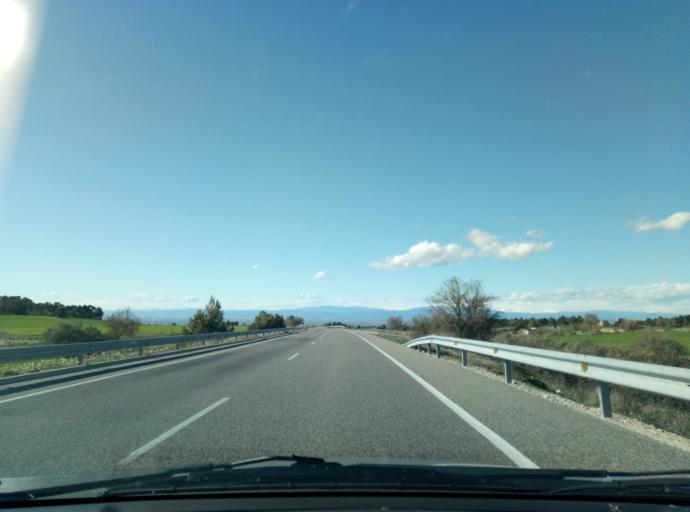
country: ES
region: Catalonia
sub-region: Provincia de Lleida
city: Ciutadilla
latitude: 41.5393
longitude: 1.1490
